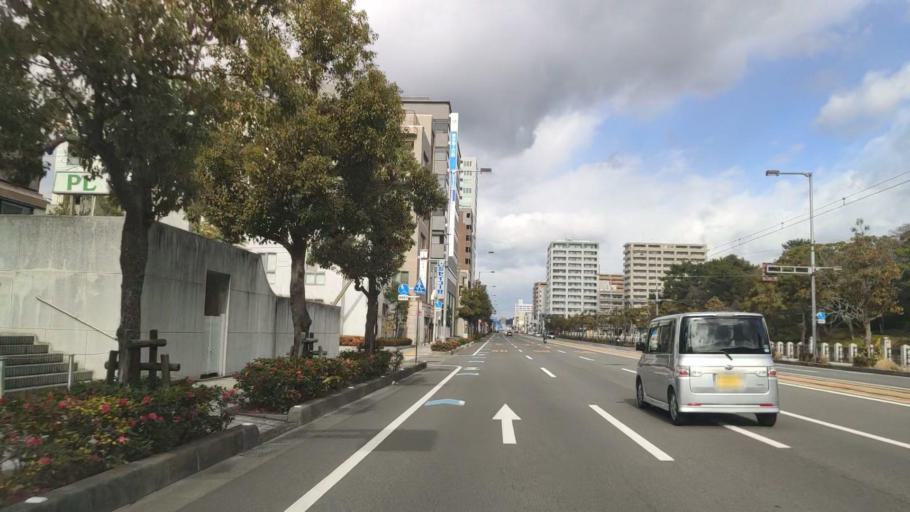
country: JP
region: Ehime
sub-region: Shikoku-chuo Shi
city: Matsuyama
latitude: 33.8422
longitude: 132.7586
